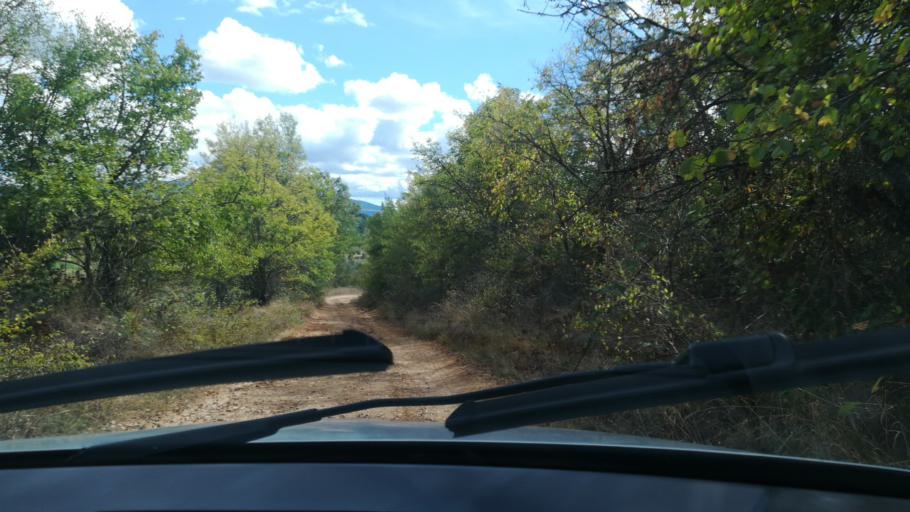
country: MK
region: Delcevo
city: Delcevo
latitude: 41.8899
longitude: 22.8047
